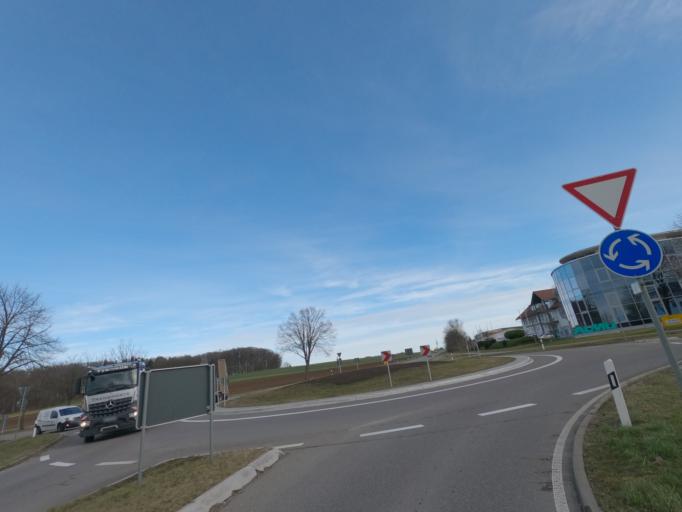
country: DE
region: Baden-Wuerttemberg
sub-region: Regierungsbezirk Stuttgart
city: Zell unter Aichelberg
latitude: 48.6525
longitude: 9.5671
